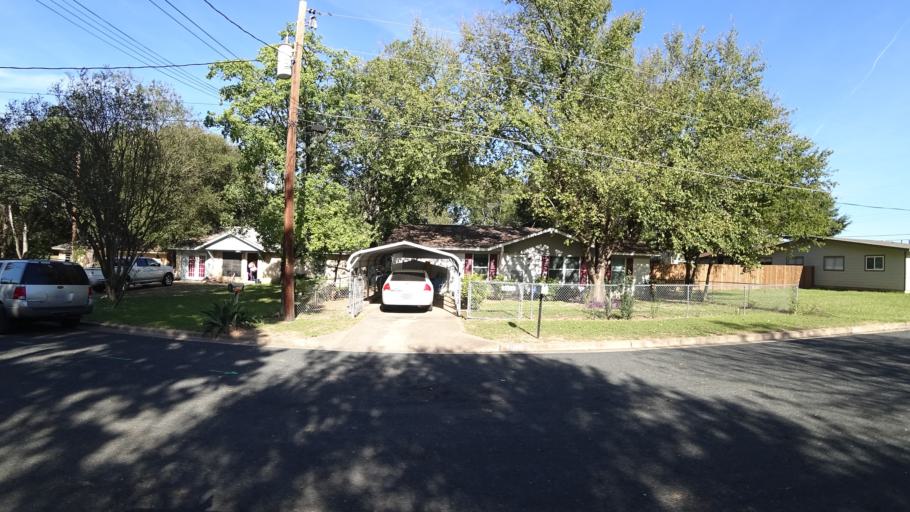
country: US
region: Texas
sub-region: Travis County
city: Austin
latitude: 30.2619
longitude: -97.6805
